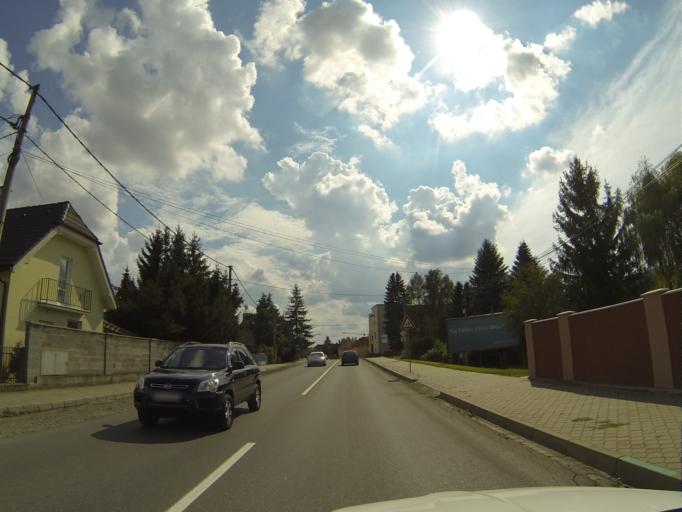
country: SK
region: Nitriansky
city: Novaky
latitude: 48.6873
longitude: 18.5267
